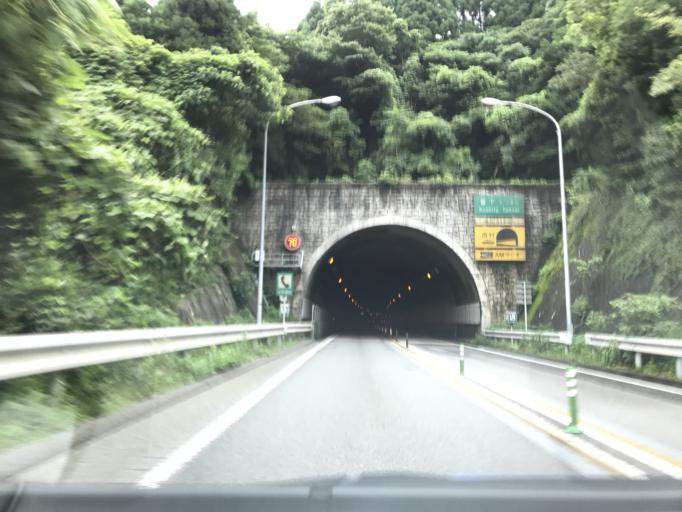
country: JP
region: Oita
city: Bungo-Takada-shi
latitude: 33.4893
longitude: 131.3247
